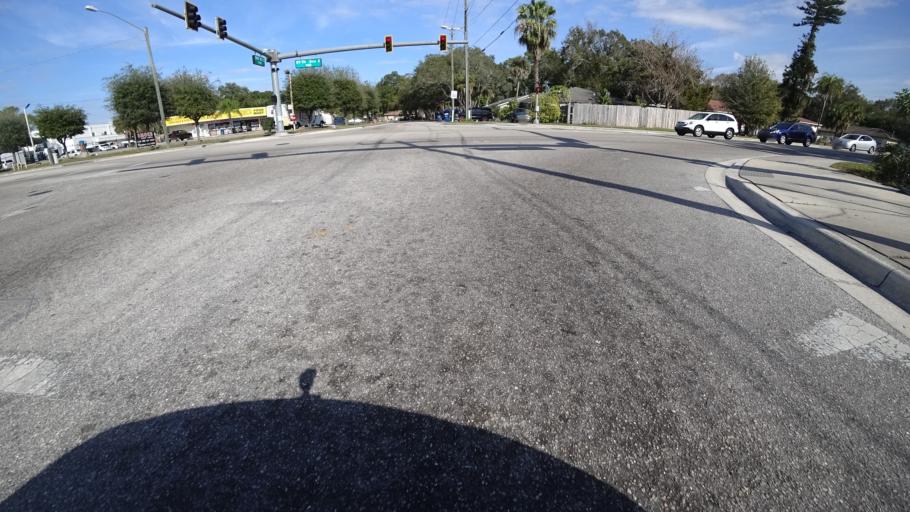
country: US
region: Florida
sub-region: Manatee County
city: Whitfield
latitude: 27.4401
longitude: -82.5590
